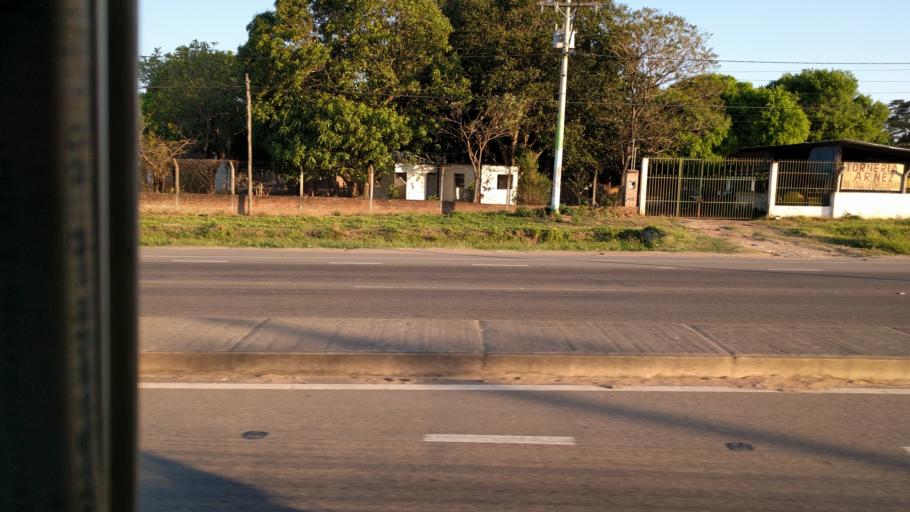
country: BO
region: Santa Cruz
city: Cotoca
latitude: -17.7643
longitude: -63.0345
